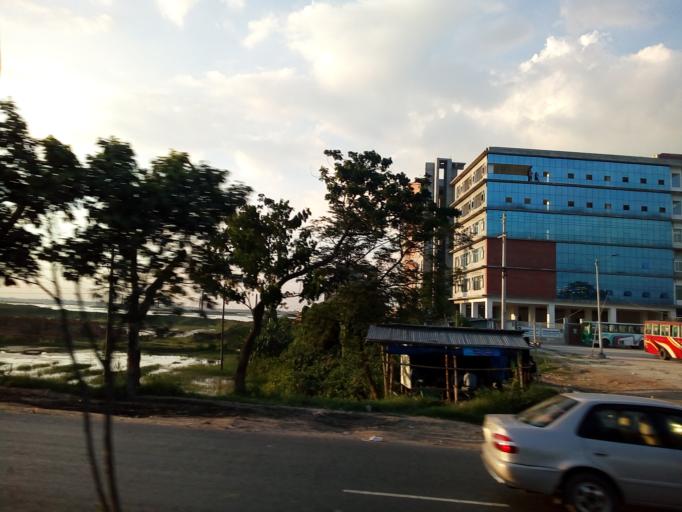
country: BD
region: Dhaka
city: Azimpur
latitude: 23.7905
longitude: 90.3156
